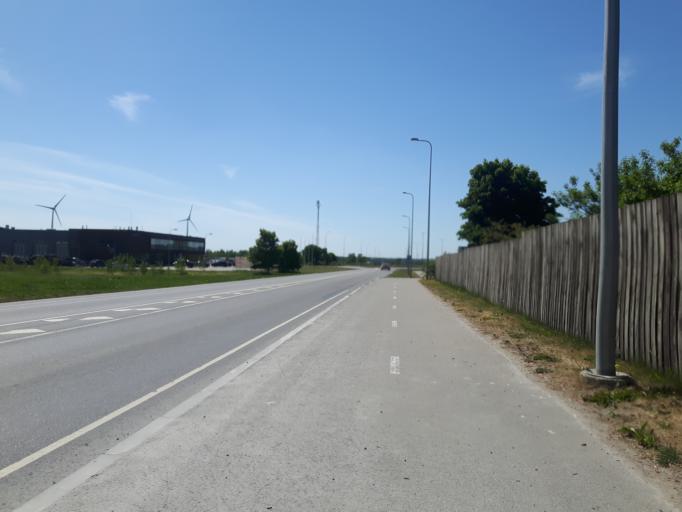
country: EE
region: Laeaene-Virumaa
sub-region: Viru-Nigula vald
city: Kunda
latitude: 59.4957
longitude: 26.5147
